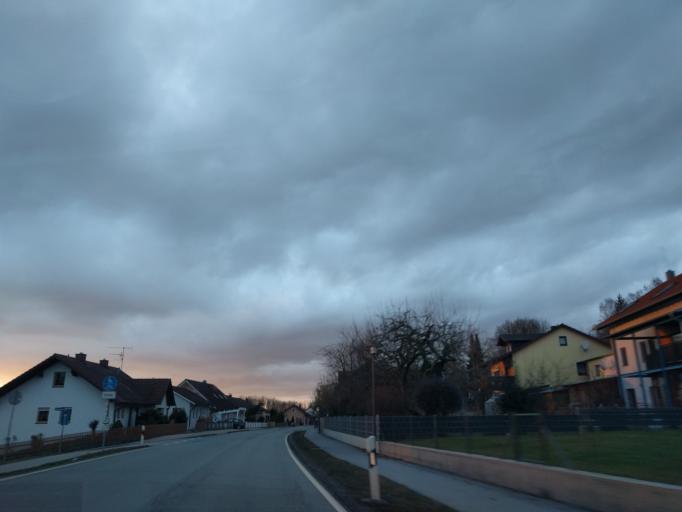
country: DE
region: Bavaria
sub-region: Lower Bavaria
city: Winzer
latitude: 48.7197
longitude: 13.0835
